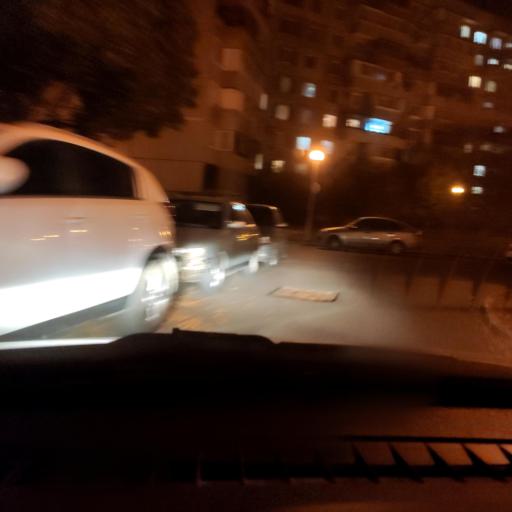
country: RU
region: Samara
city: Tol'yatti
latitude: 53.5452
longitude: 49.3367
